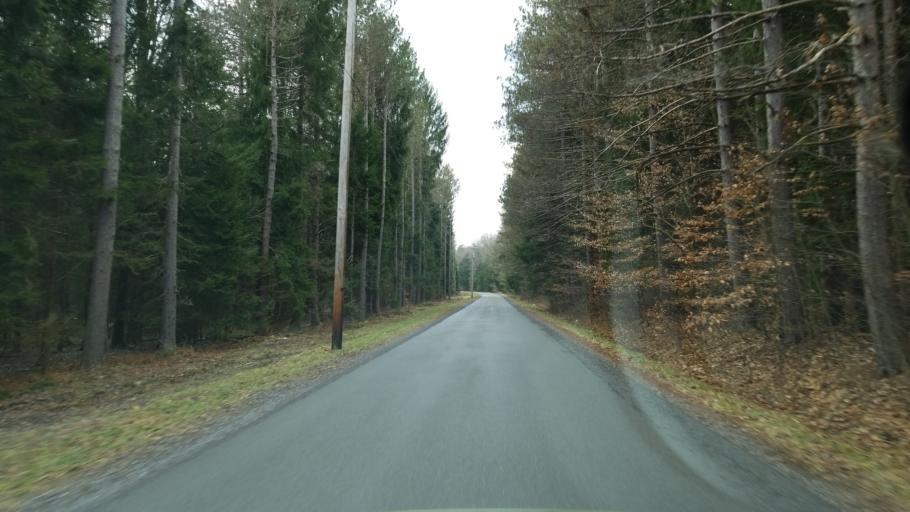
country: US
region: Pennsylvania
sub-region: Clearfield County
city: Treasure Lake
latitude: 41.1476
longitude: -78.5612
